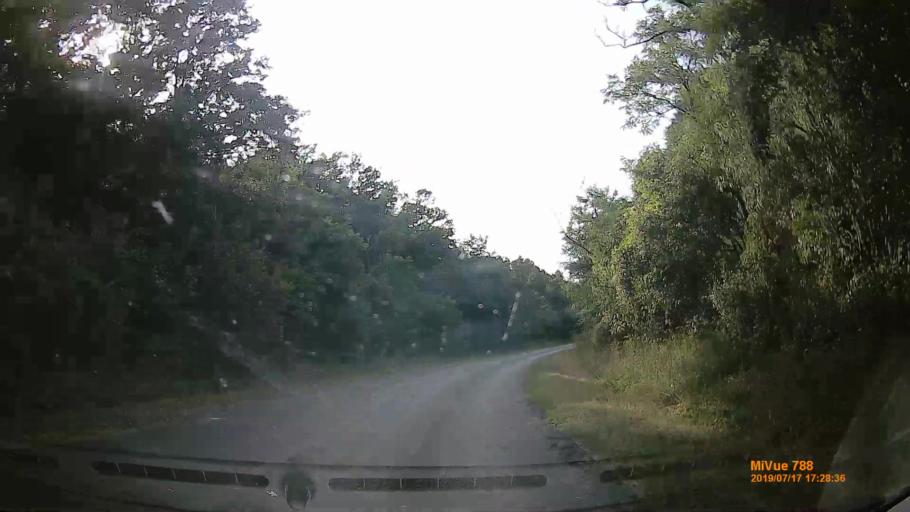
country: HU
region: Veszprem
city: Urkut
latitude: 47.0087
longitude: 17.5936
